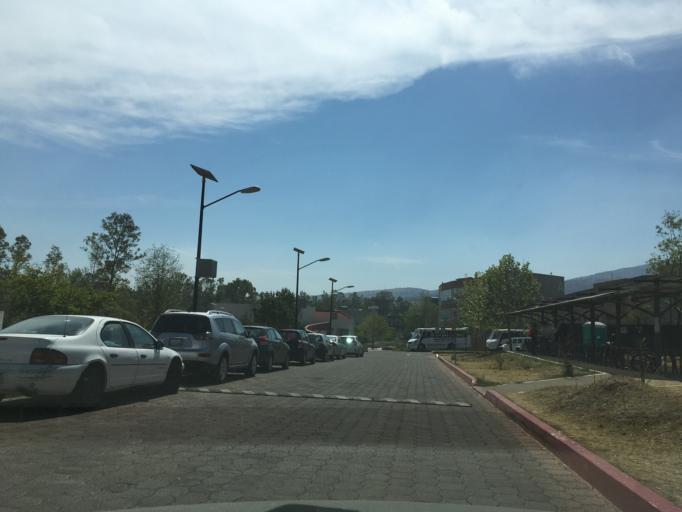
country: MX
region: Michoacan
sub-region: Morelia
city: Morelos
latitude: 19.6504
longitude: -101.2241
